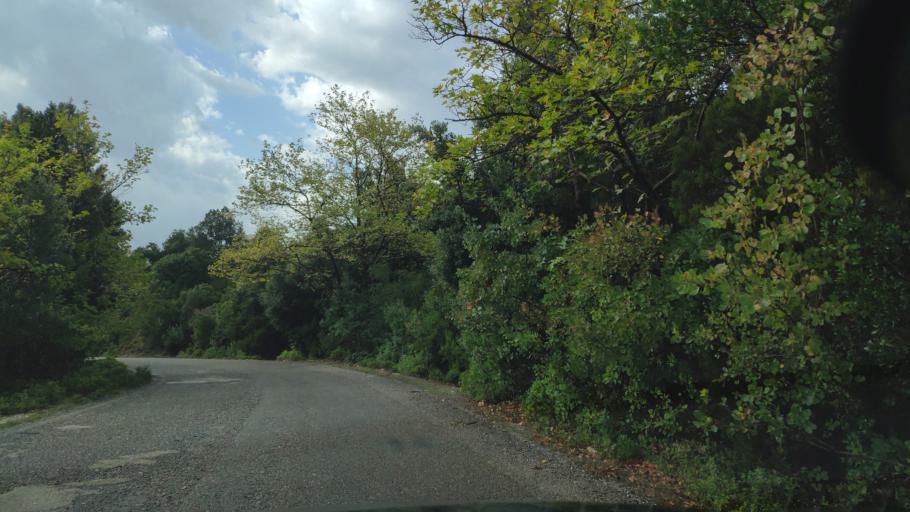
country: GR
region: West Greece
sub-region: Nomos Aitolias kai Akarnanias
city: Sardinia
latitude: 38.8577
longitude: 21.3062
